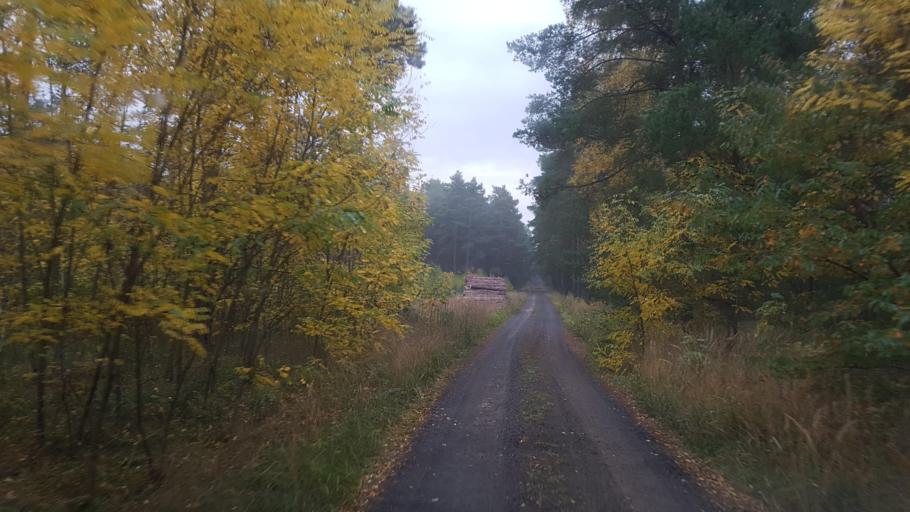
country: DE
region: Brandenburg
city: Schlieben
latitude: 51.7412
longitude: 13.3900
